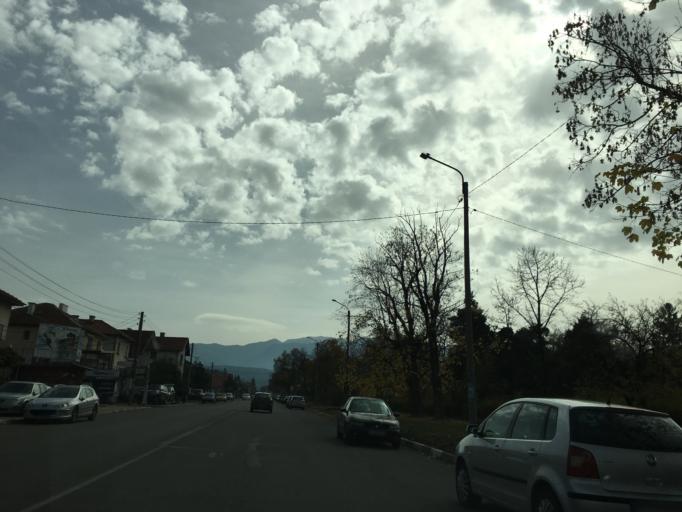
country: BG
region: Sofiya
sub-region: Obshtina Samokov
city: Samokov
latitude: 42.3250
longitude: 23.5603
